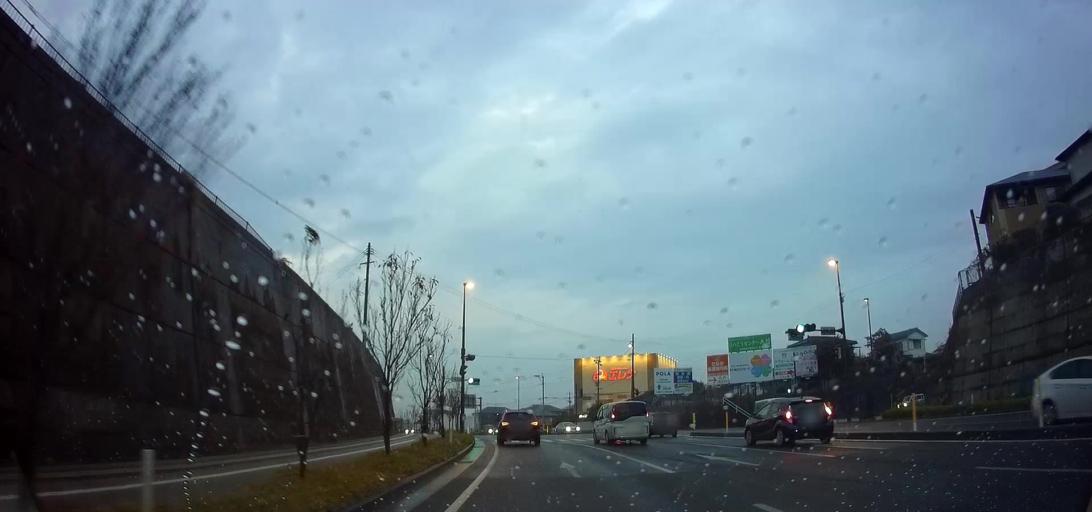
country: JP
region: Nagasaki
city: Omura
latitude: 32.8938
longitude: 129.9688
